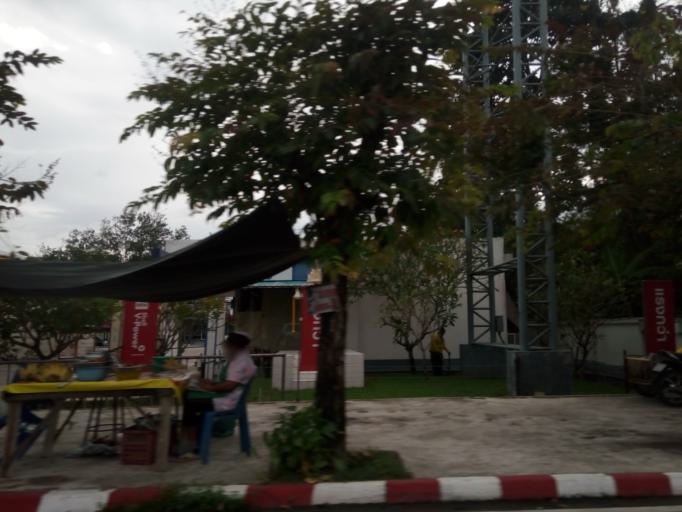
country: TH
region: Phuket
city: Ban Ko Kaeo
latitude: 7.9810
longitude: 98.3635
